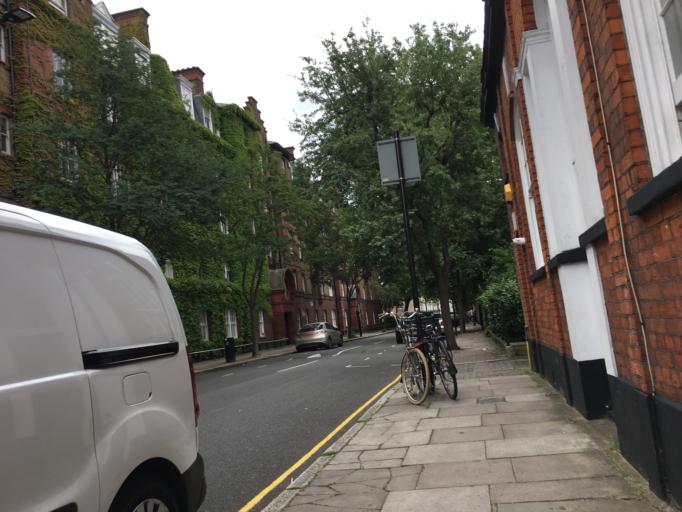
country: GB
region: England
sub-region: Greater London
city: Barnsbury
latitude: 51.5435
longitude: -0.1109
